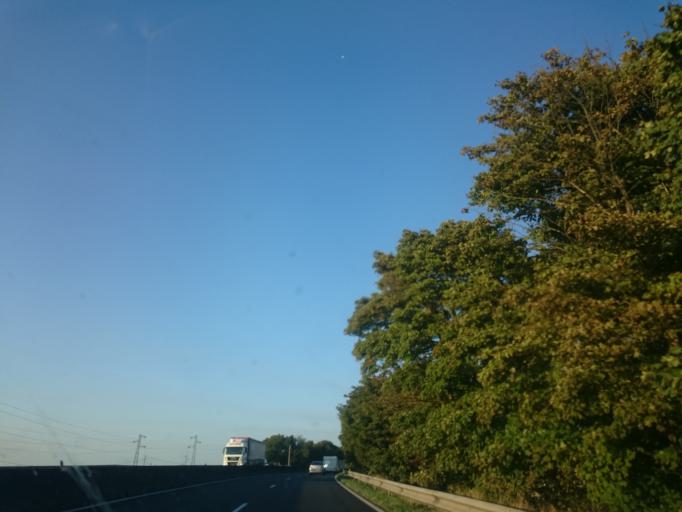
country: FR
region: Ile-de-France
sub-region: Departement de l'Essonne
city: Angerville
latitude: 48.3167
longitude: 1.9956
